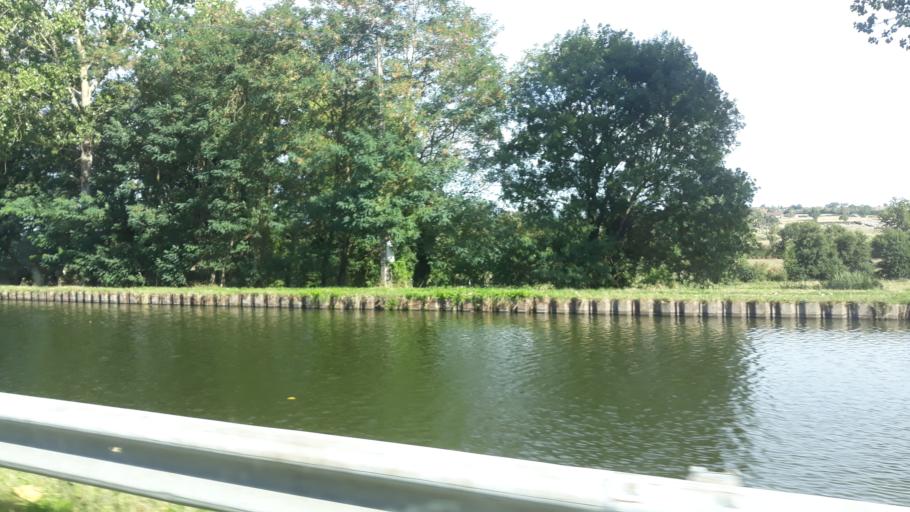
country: FR
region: Bourgogne
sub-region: Departement de Saone-et-Loire
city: Ecuisses
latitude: 46.7662
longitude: 4.5245
